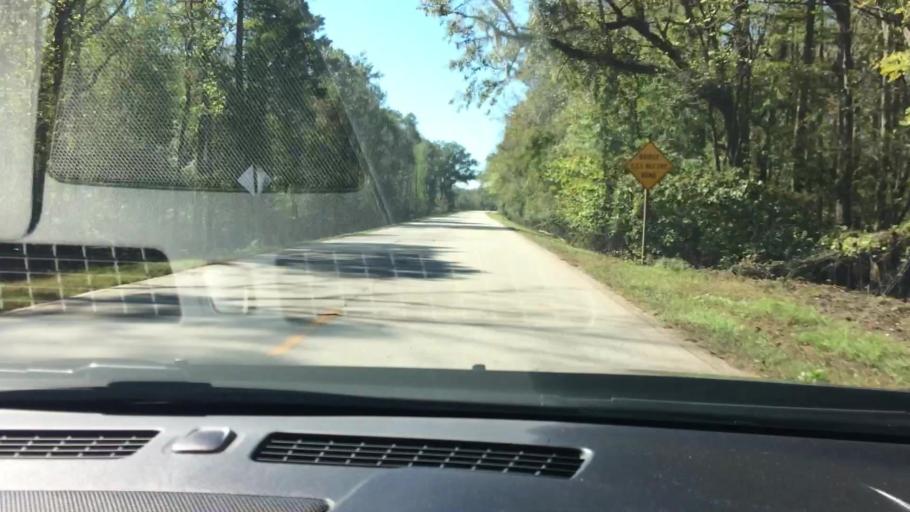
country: US
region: North Carolina
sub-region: Craven County
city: Vanceboro
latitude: 35.3170
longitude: -77.2964
